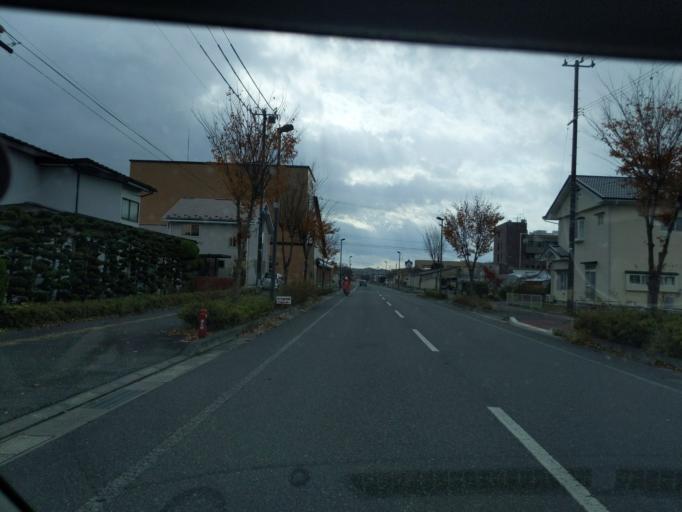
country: JP
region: Iwate
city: Mizusawa
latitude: 39.0530
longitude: 141.1252
